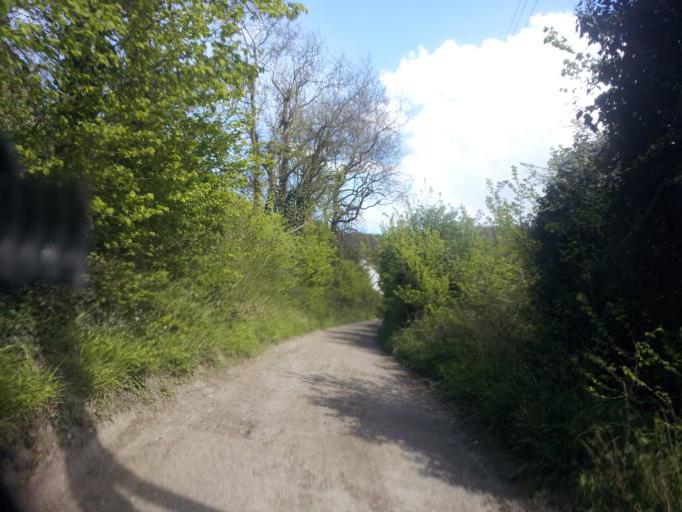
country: GB
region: England
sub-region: Kent
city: Boxley
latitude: 51.3197
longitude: 0.5146
